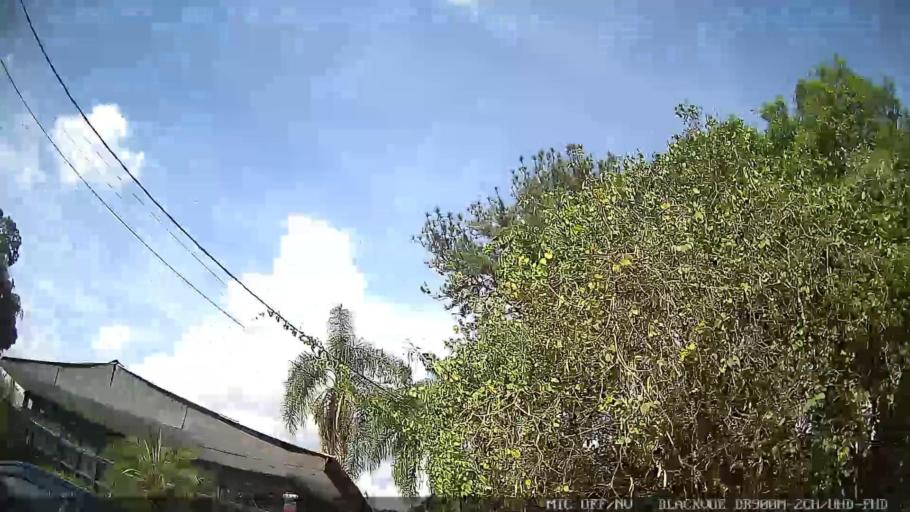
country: BR
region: Sao Paulo
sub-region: Braganca Paulista
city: Braganca Paulista
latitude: -22.9795
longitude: -46.5316
